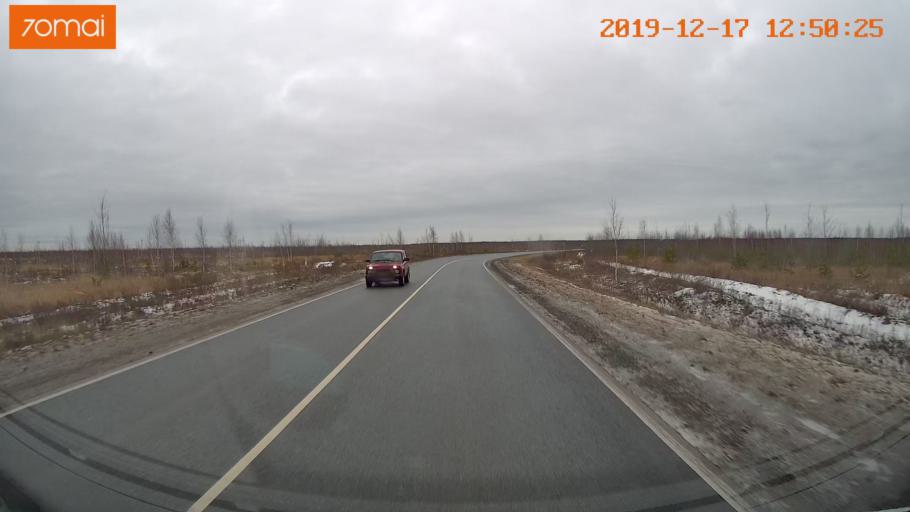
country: RU
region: Rjazan
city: Solotcha
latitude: 54.8702
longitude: 39.9841
